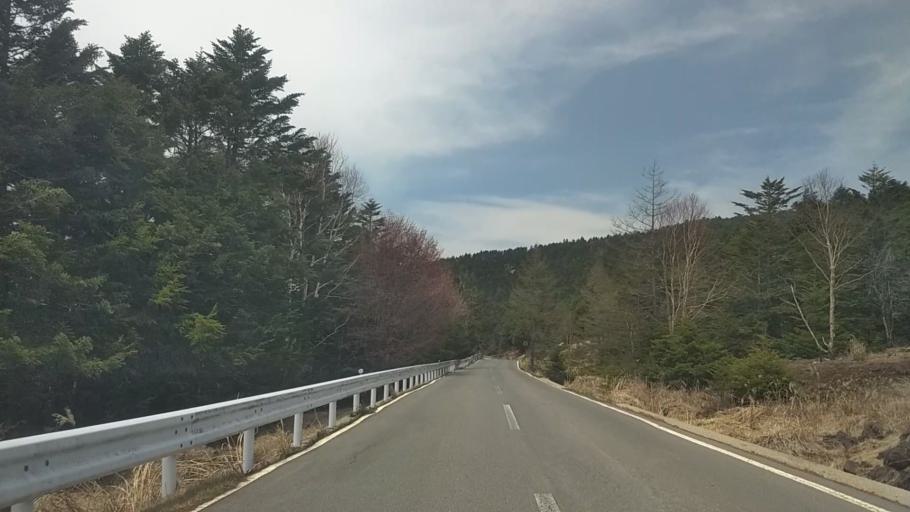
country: JP
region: Nagano
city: Chino
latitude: 36.0573
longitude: 138.3267
